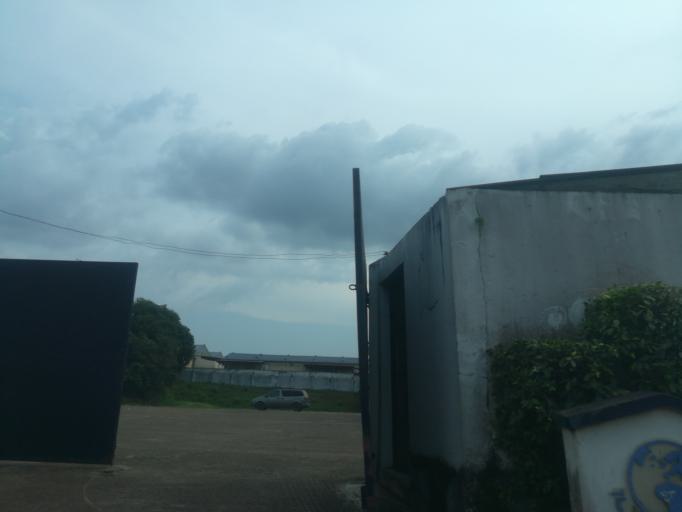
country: NG
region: Oyo
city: Ibadan
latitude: 7.3676
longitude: 3.8549
